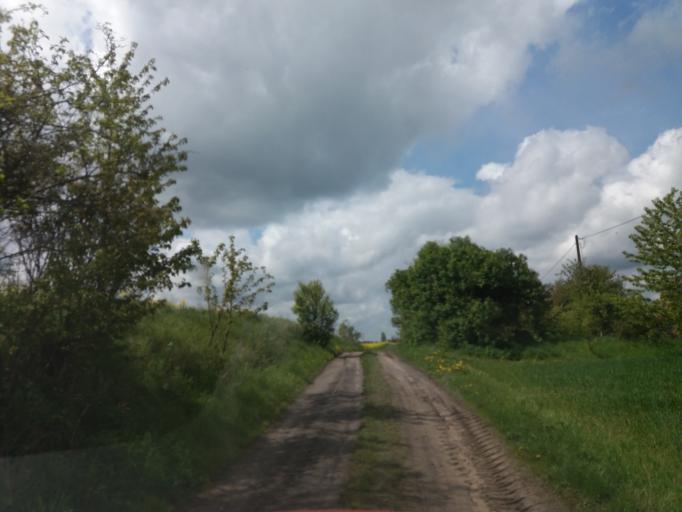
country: PL
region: West Pomeranian Voivodeship
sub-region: Powiat choszczenski
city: Choszczno
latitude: 53.1991
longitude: 15.4039
